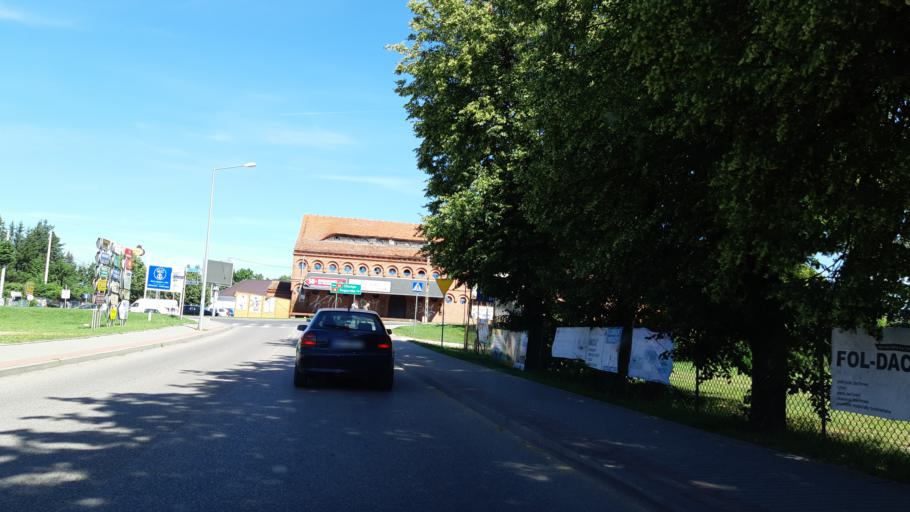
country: PL
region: Warmian-Masurian Voivodeship
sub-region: Powiat mragowski
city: Mikolajki
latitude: 53.8039
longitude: 21.5735
